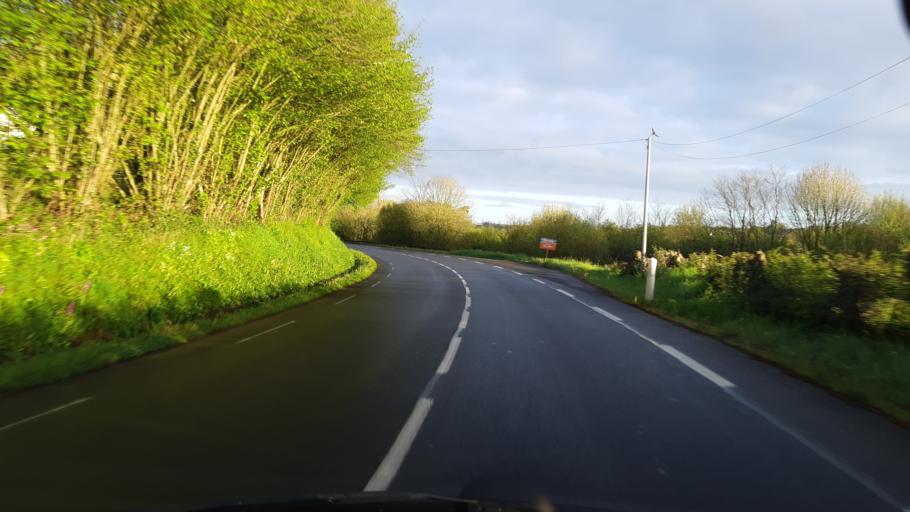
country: FR
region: Lower Normandy
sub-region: Departement de la Manche
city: Agneaux
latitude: 49.0876
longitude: -1.1147
